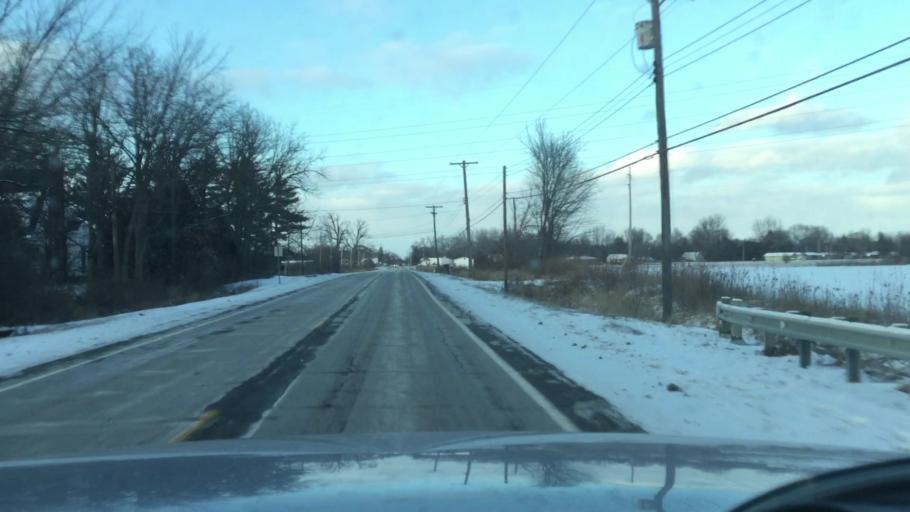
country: US
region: Michigan
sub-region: Saginaw County
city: Saginaw
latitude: 43.3857
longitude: -83.9356
